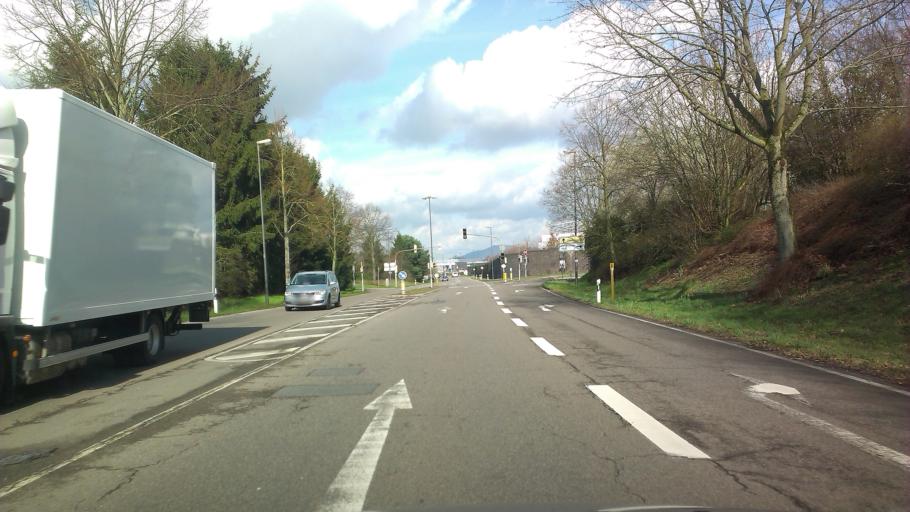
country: DE
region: Baden-Wuerttemberg
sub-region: Karlsruhe Region
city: Eppelheim
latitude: 49.3801
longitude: 8.6563
